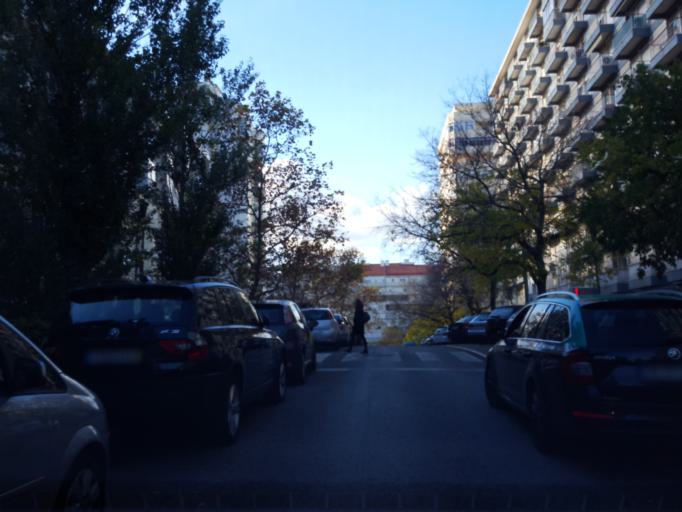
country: PT
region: Lisbon
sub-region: Odivelas
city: Pontinha
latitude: 38.7471
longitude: -9.1858
